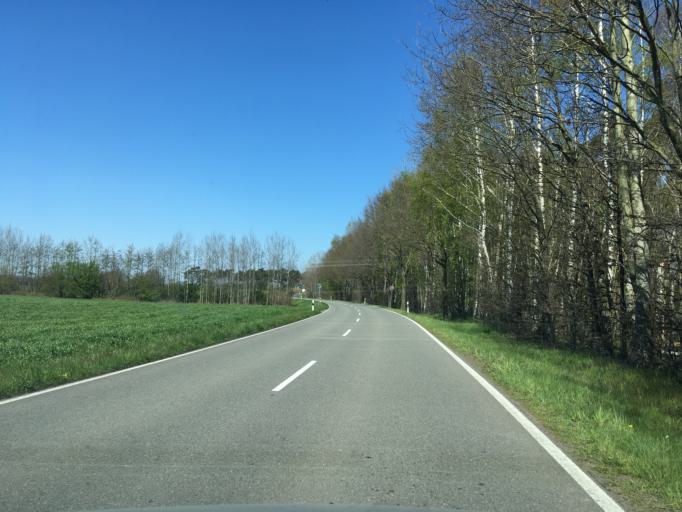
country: DE
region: North Rhine-Westphalia
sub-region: Regierungsbezirk Munster
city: Vreden
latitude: 51.9989
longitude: 6.8489
